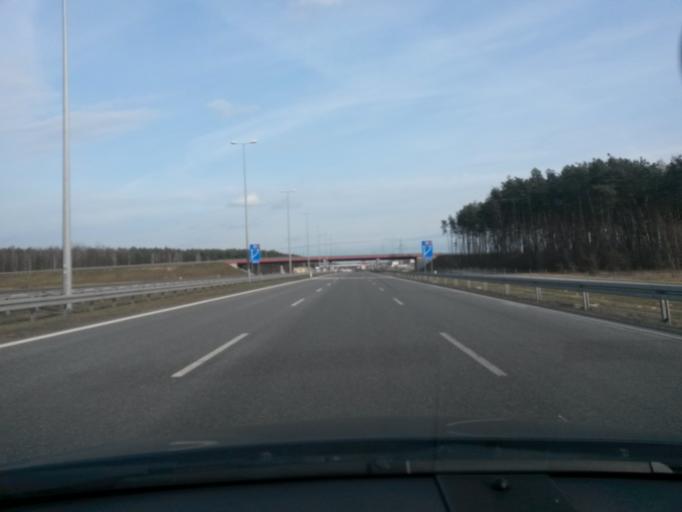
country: PL
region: Greater Poland Voivodeship
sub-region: Powiat koninski
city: Stare Miasto
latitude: 52.1551
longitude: 18.2691
